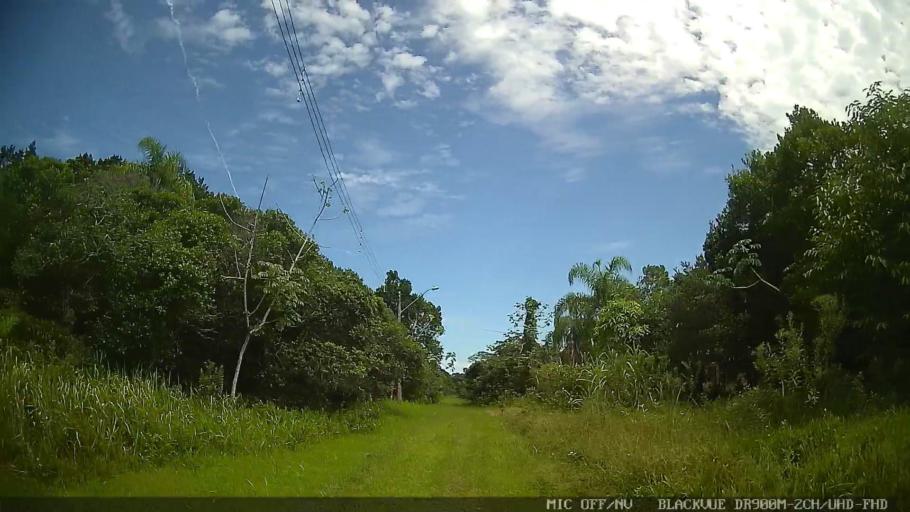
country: BR
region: Sao Paulo
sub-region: Iguape
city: Iguape
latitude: -24.7203
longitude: -47.5303
